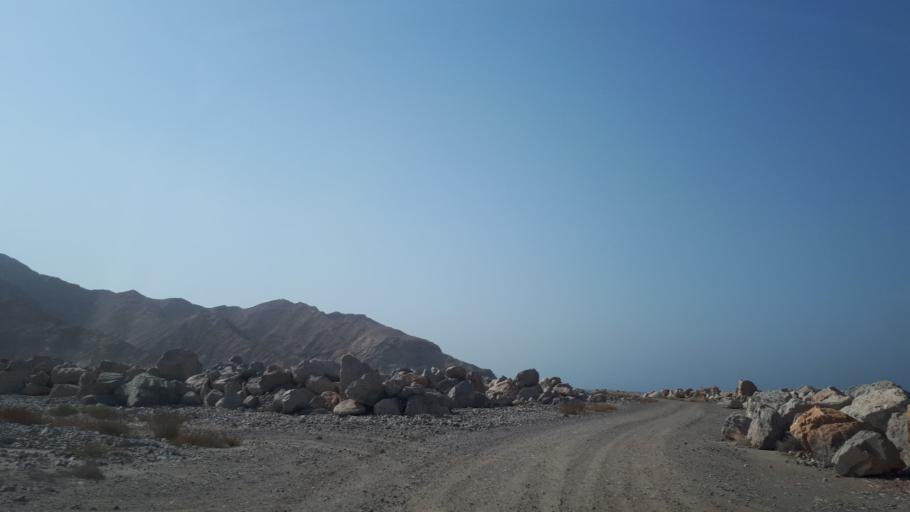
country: OM
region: Muhafazat Masqat
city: Muscat
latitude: 23.5401
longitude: 58.6693
